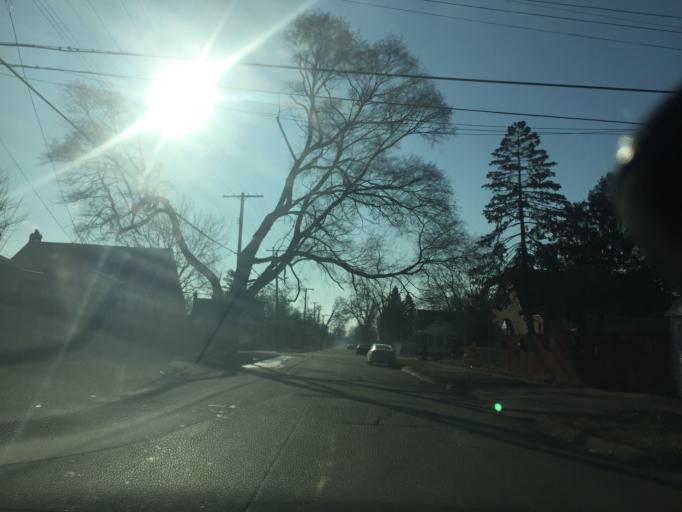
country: US
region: Michigan
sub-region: Macomb County
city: Eastpointe
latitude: 42.4415
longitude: -82.9584
